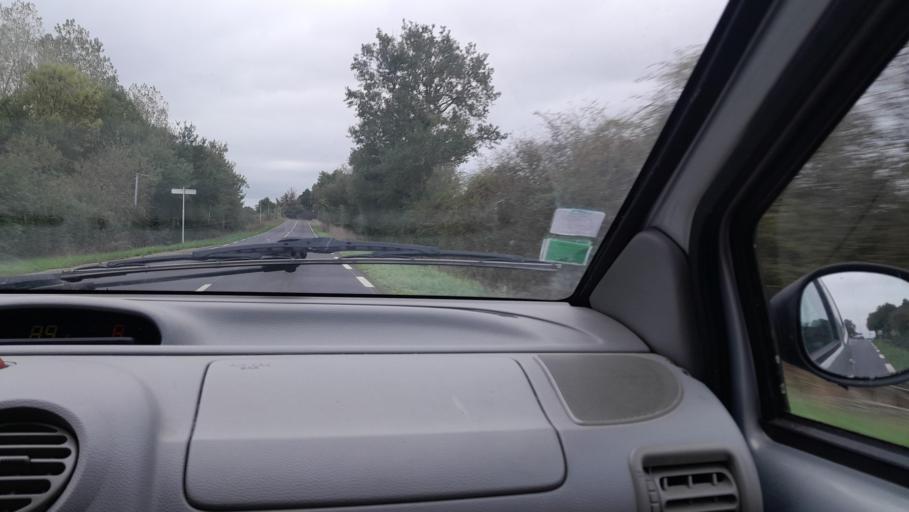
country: FR
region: Pays de la Loire
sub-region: Departement de la Loire-Atlantique
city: Saint-Mars-la-Jaille
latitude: 47.5989
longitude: -1.1992
